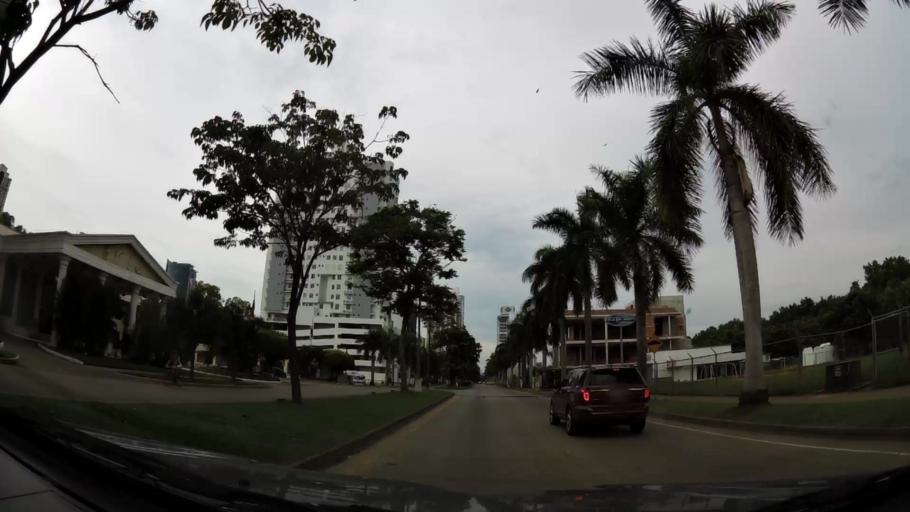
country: PA
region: Panama
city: San Miguelito
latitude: 9.0161
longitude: -79.4715
